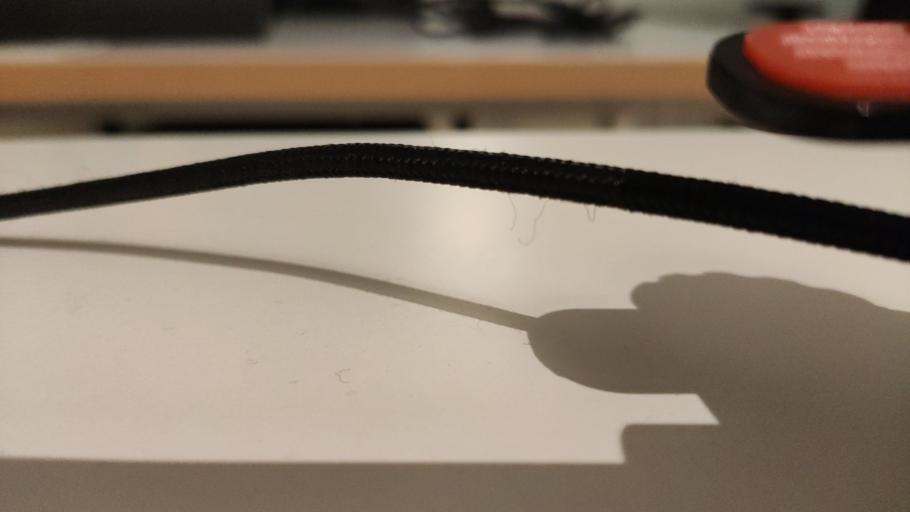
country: RU
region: Moskovskaya
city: Novosin'kovo
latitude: 56.3926
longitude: 37.2879
